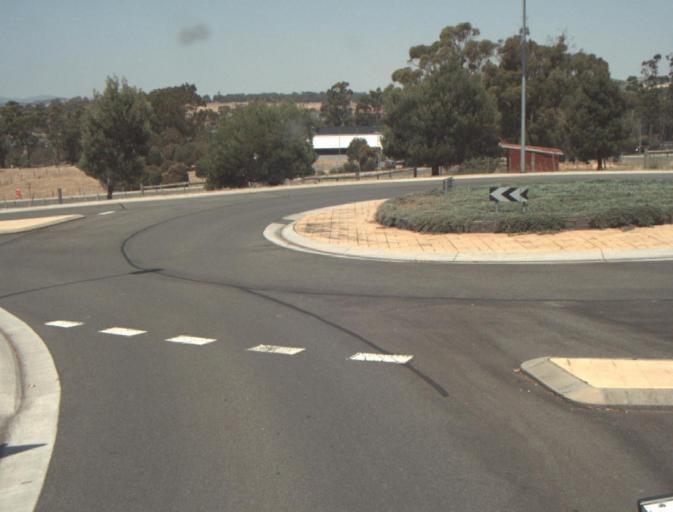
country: AU
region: Tasmania
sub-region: Launceston
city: Newstead
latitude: -41.4734
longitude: 147.1750
